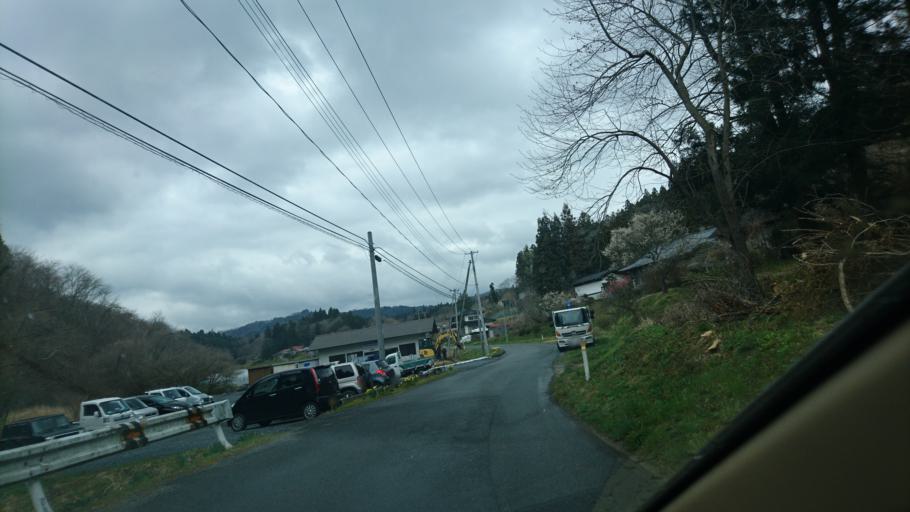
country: JP
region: Iwate
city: Ichinoseki
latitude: 38.9430
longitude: 141.3246
